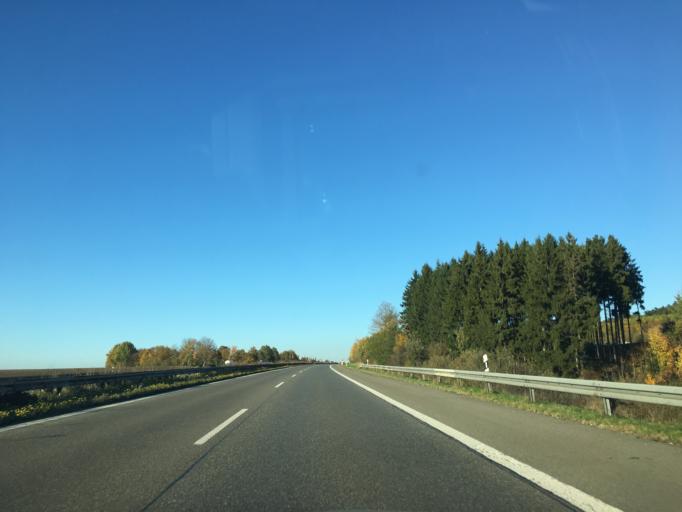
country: DE
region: Baden-Wuerttemberg
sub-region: Freiburg Region
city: Tuningen
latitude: 48.0118
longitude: 8.6063
